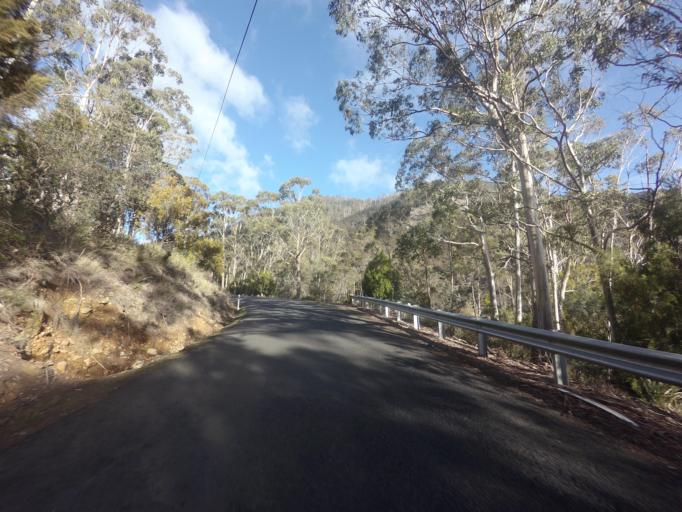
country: AU
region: Tasmania
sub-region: Glenorchy
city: Berriedale
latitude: -42.8150
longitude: 147.1756
